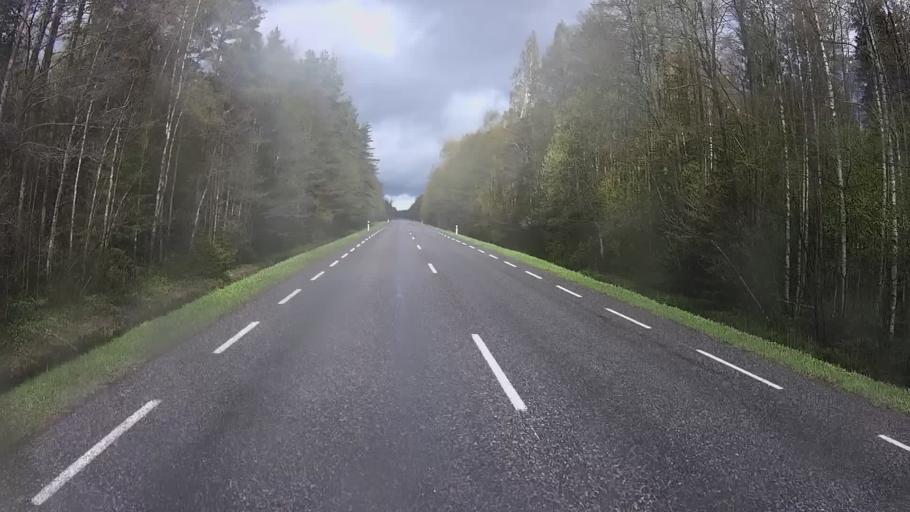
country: EE
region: Hiiumaa
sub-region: Kaerdla linn
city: Kardla
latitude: 58.9060
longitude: 22.9292
